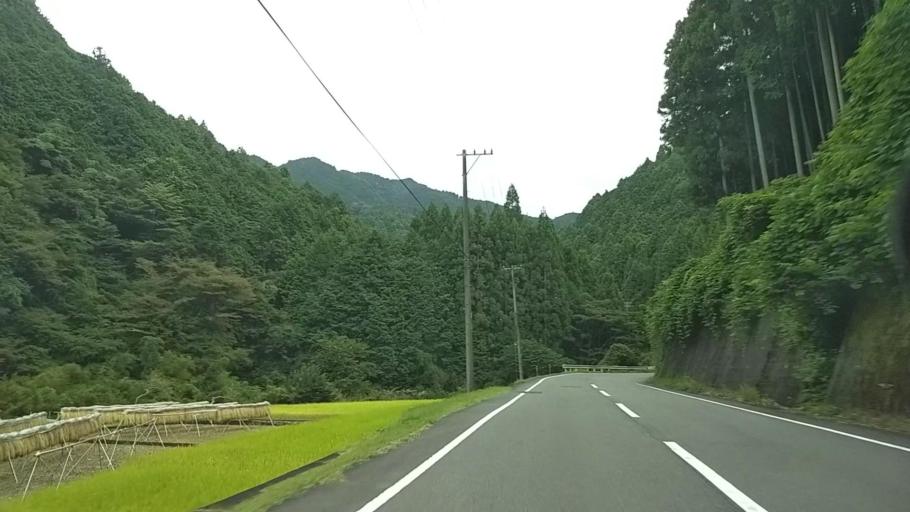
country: JP
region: Shizuoka
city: Fujinomiya
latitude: 35.1632
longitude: 138.5390
